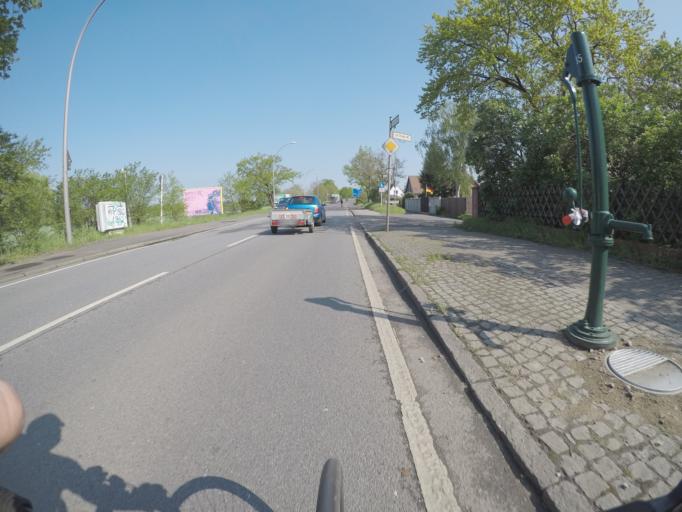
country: DE
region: Berlin
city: Buchholz
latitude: 52.6190
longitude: 13.4307
